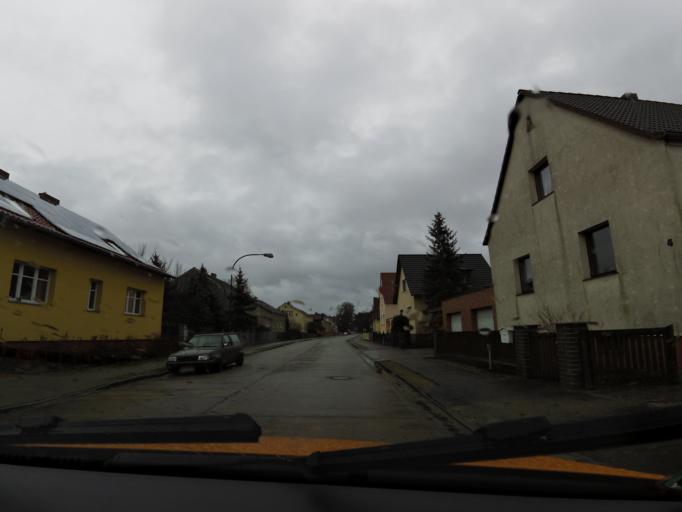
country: DE
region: Brandenburg
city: Sperenberg
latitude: 52.1665
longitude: 13.3646
